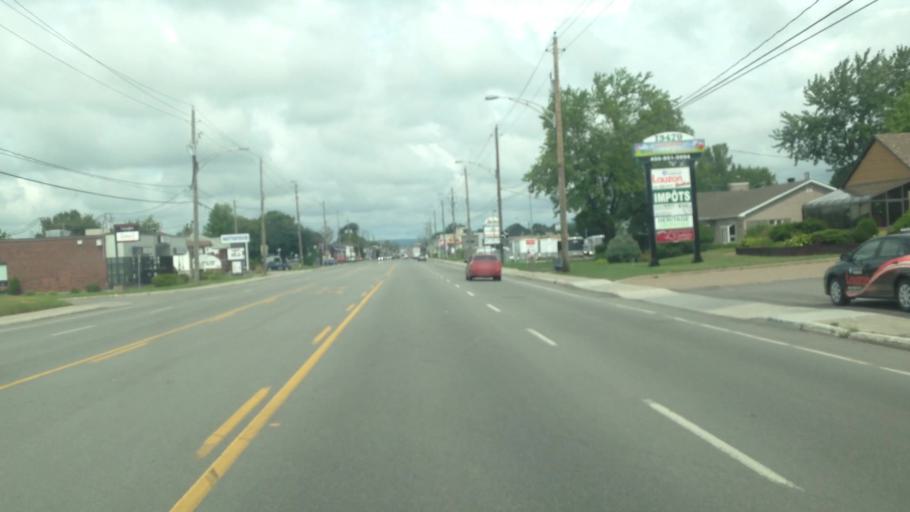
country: CA
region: Quebec
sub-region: Laurentides
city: Blainville
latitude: 45.7001
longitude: -73.9214
